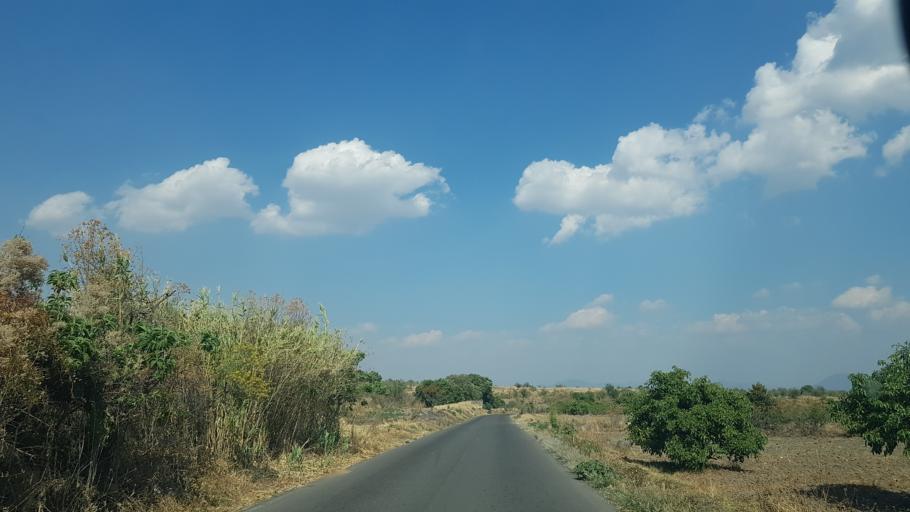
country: MX
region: Puebla
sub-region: Atlixco
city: Colonia Agricola de Ocotepec (Colonia San Jose)
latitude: 18.9210
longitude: -98.5359
